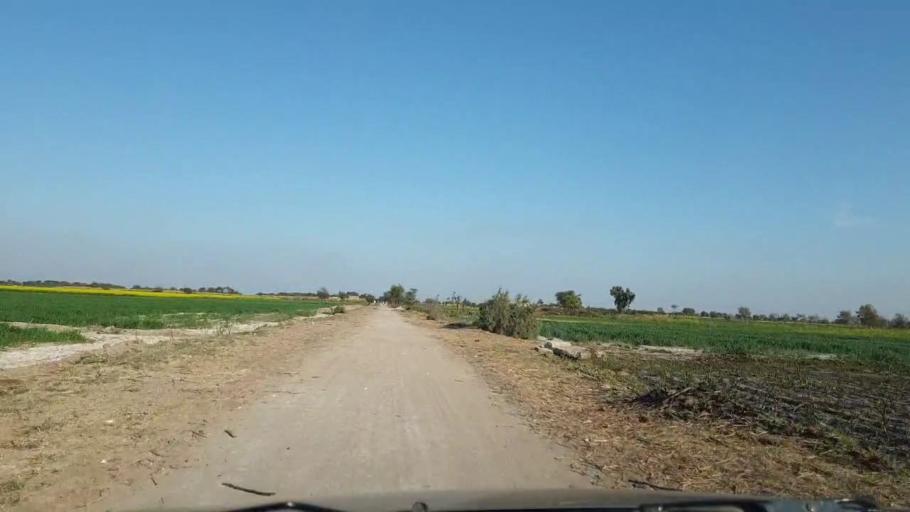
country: PK
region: Sindh
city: Khadro
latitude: 26.2034
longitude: 68.7559
